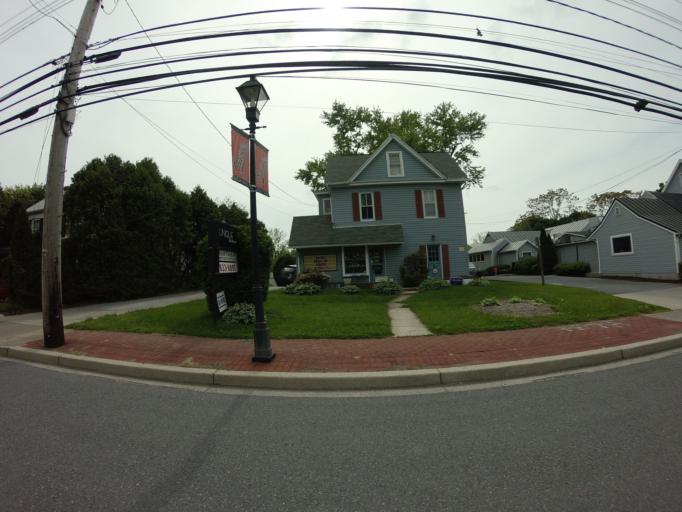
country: US
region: Maryland
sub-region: Baltimore County
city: Reisterstown
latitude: 39.4606
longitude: -76.8276
